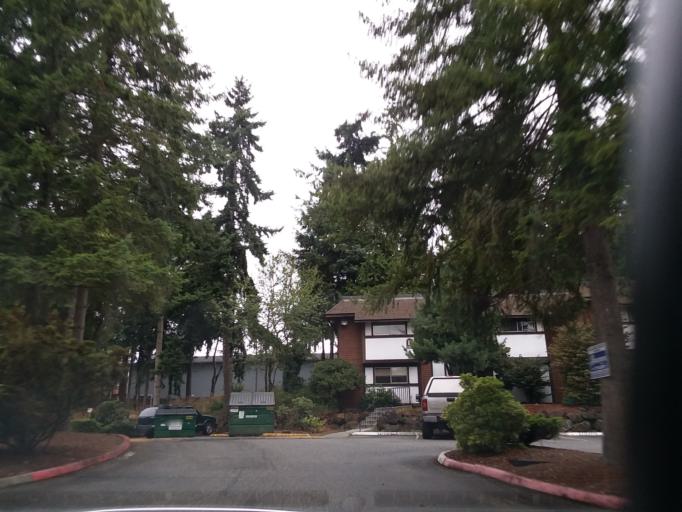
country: US
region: Washington
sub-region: Snohomish County
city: Mountlake Terrace
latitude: 47.7973
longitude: -122.3315
